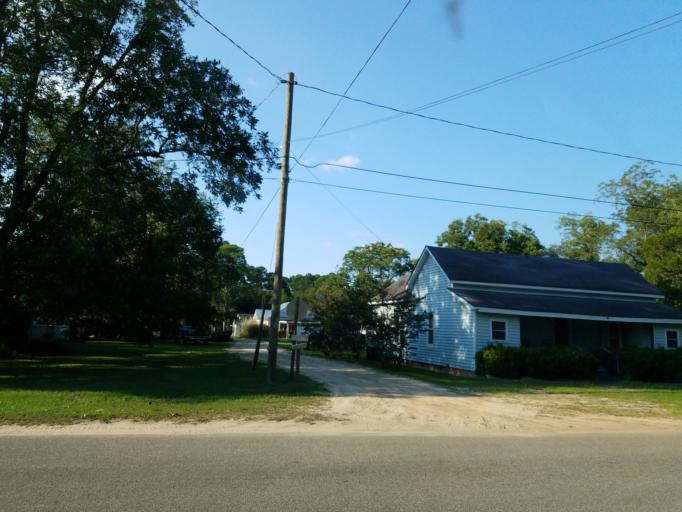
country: US
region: Georgia
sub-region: Cook County
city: Sparks
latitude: 31.2703
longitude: -83.4671
